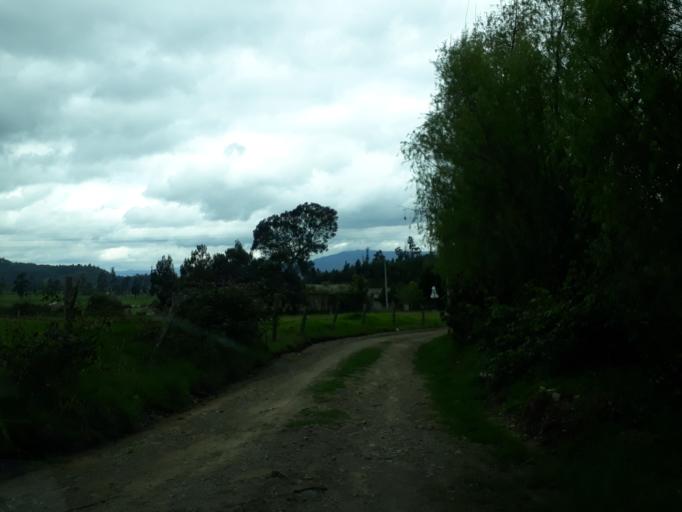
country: CO
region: Cundinamarca
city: Guacheta
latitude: 5.4366
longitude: -73.7109
